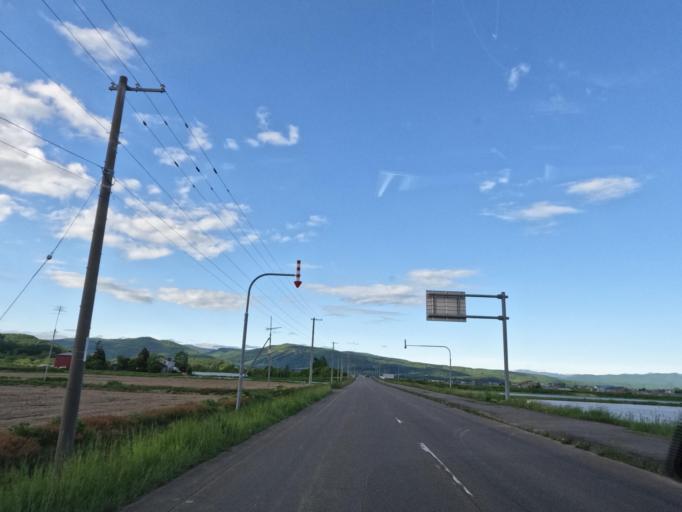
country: JP
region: Hokkaido
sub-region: Asahikawa-shi
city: Asahikawa
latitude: 43.8863
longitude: 142.4608
